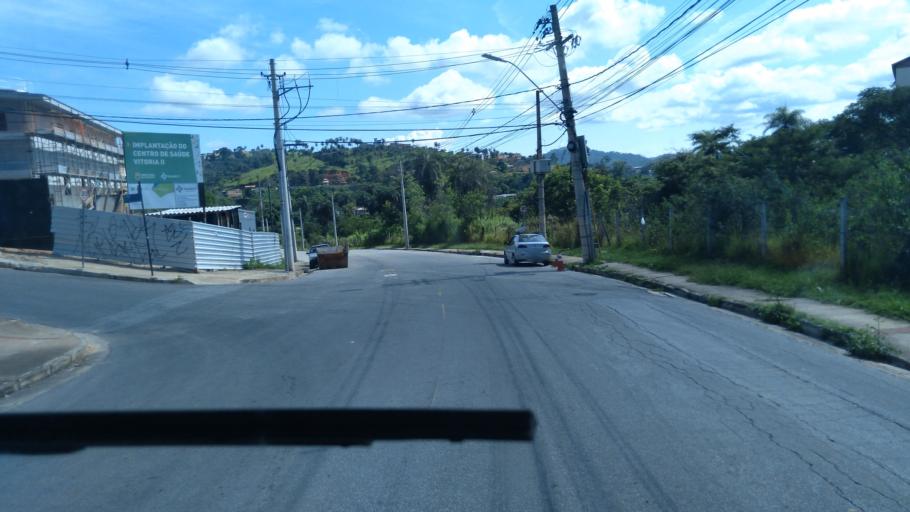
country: BR
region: Minas Gerais
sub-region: Santa Luzia
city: Santa Luzia
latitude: -19.8443
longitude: -43.8791
